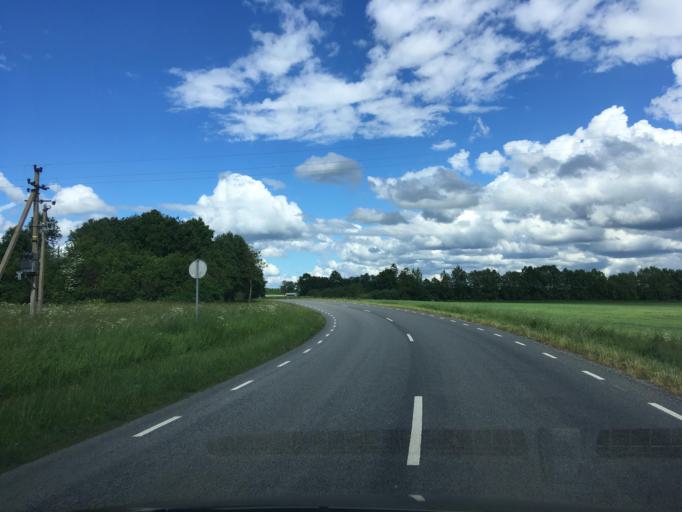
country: EE
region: Paernumaa
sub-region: Halinga vald
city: Parnu-Jaagupi
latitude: 58.6212
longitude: 24.3940
